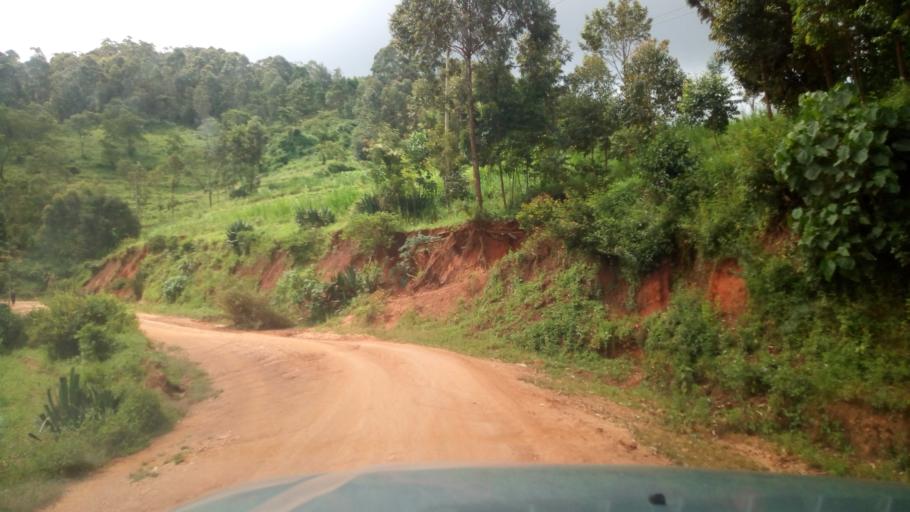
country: KE
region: Makueni
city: Wote
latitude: -1.6736
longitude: 37.4475
